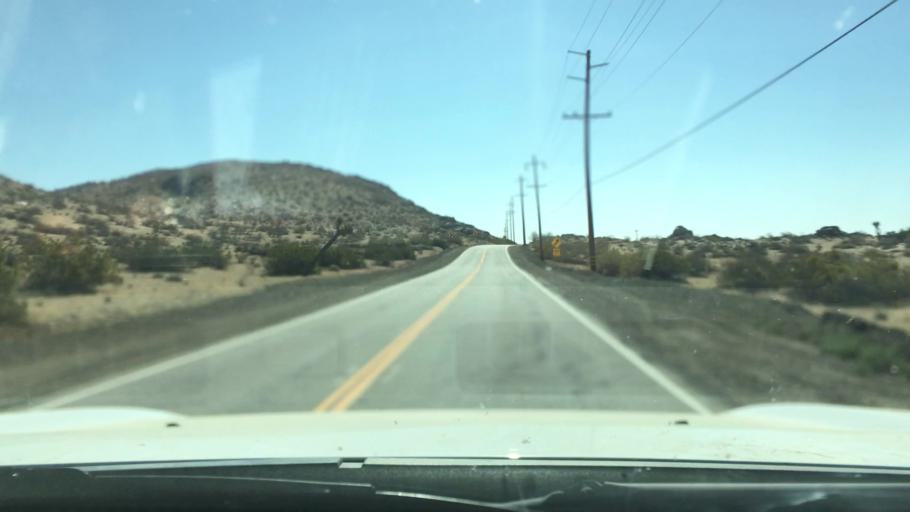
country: US
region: California
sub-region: Los Angeles County
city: Lake Los Angeles
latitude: 34.5798
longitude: -117.7360
